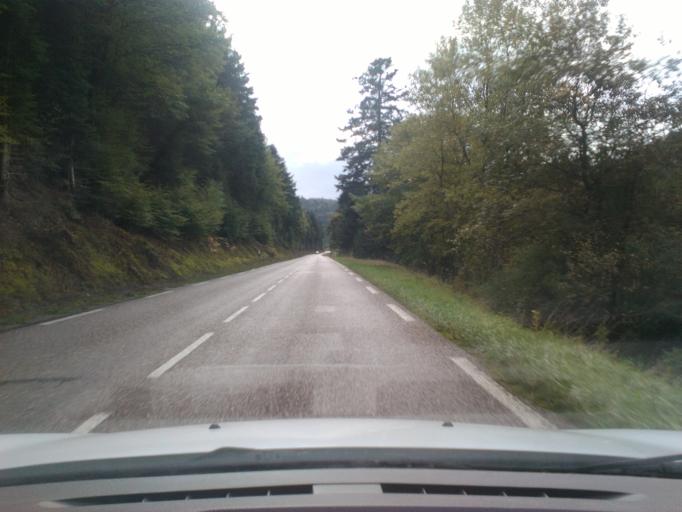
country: FR
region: Lorraine
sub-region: Departement des Vosges
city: Taintrux
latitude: 48.2680
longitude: 6.8193
